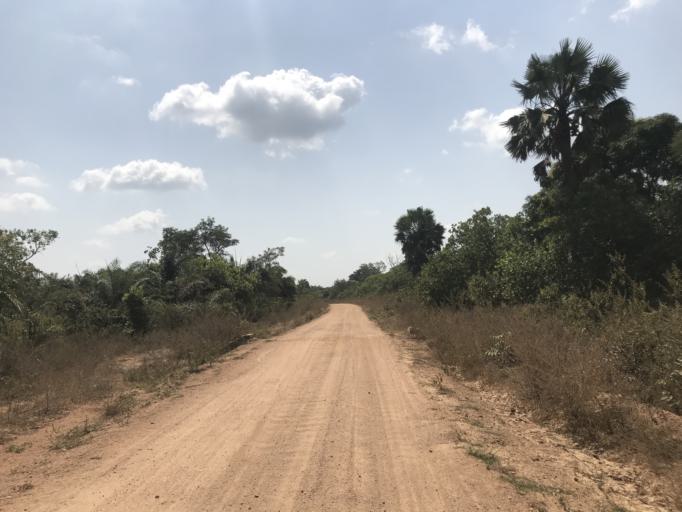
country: NG
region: Osun
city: Ifon
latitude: 7.9423
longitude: 4.4882
